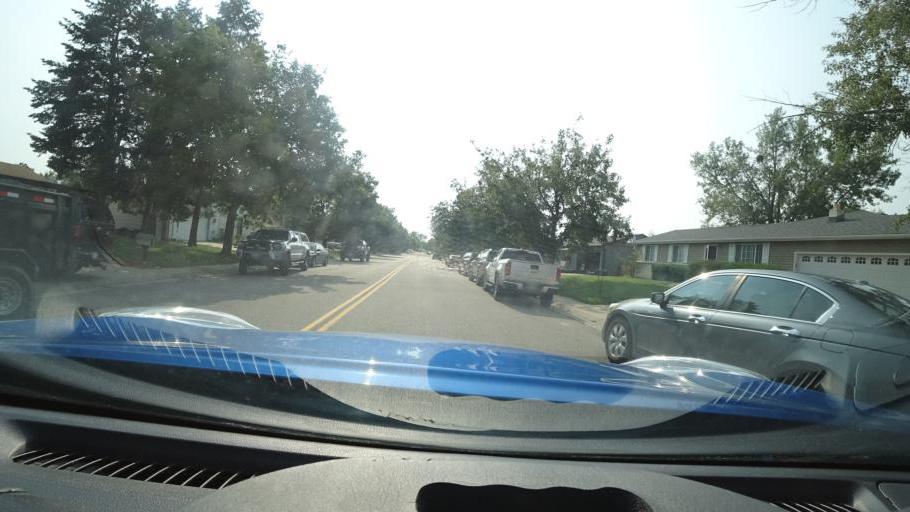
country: US
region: Colorado
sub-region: Adams County
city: Aurora
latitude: 39.6670
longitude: -104.8004
